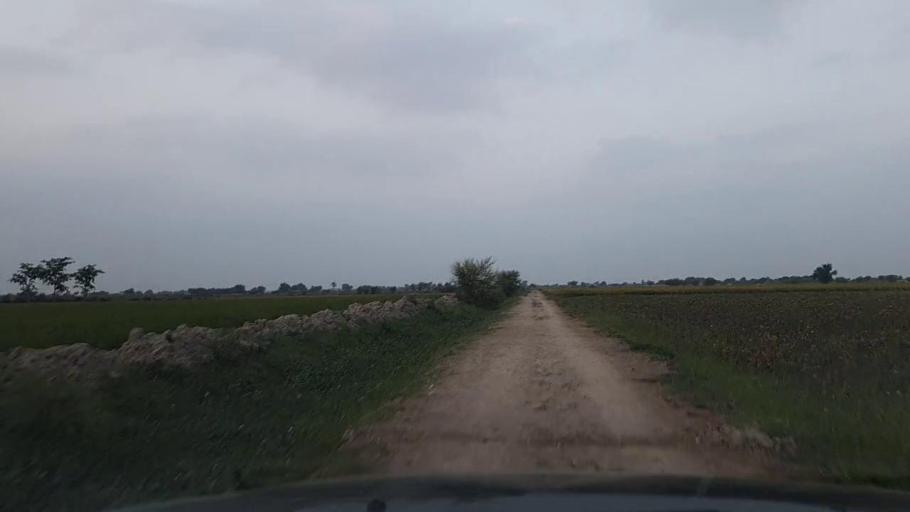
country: PK
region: Sindh
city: Jati
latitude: 24.5056
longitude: 68.3931
